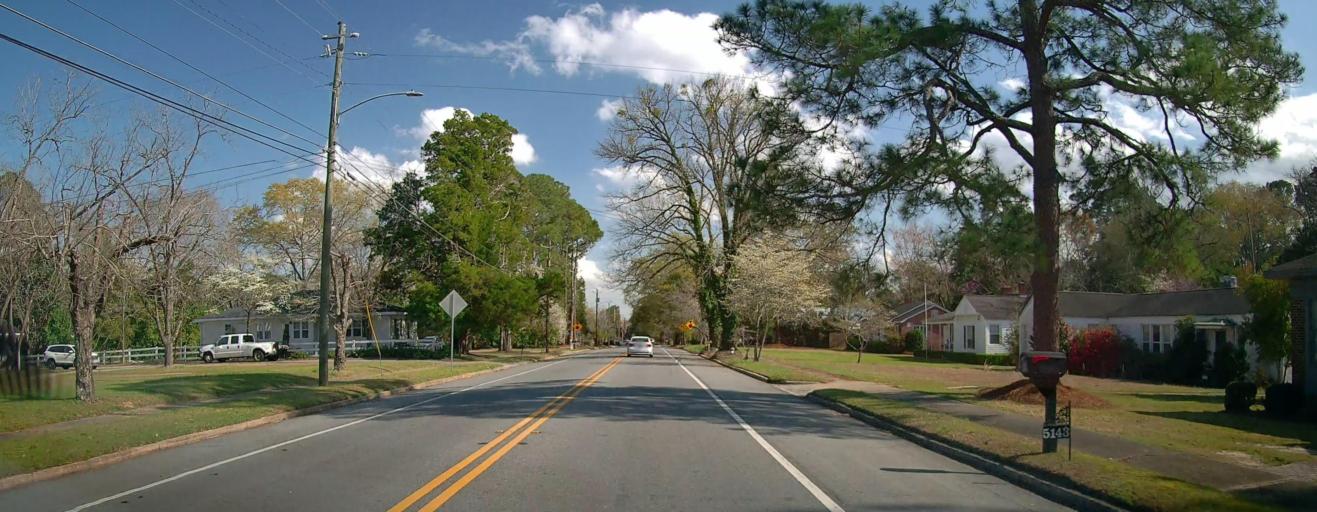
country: US
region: Georgia
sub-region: Dodge County
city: Eastman
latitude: 32.1955
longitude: -83.1845
